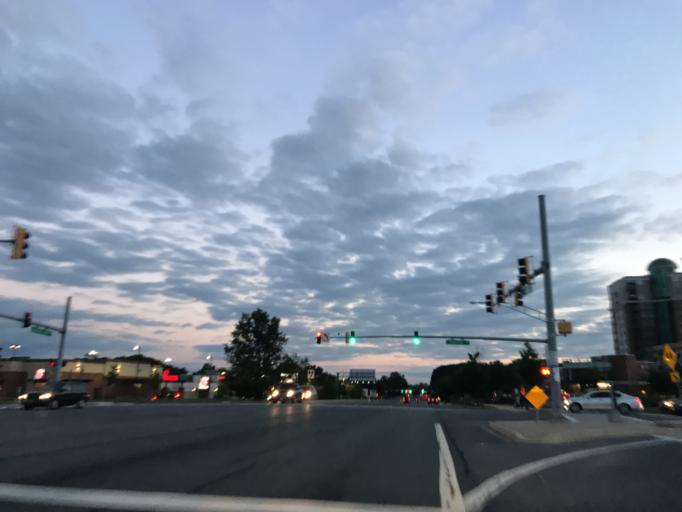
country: US
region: Maryland
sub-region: Anne Arundel County
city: Parole
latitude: 38.9816
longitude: -76.5371
